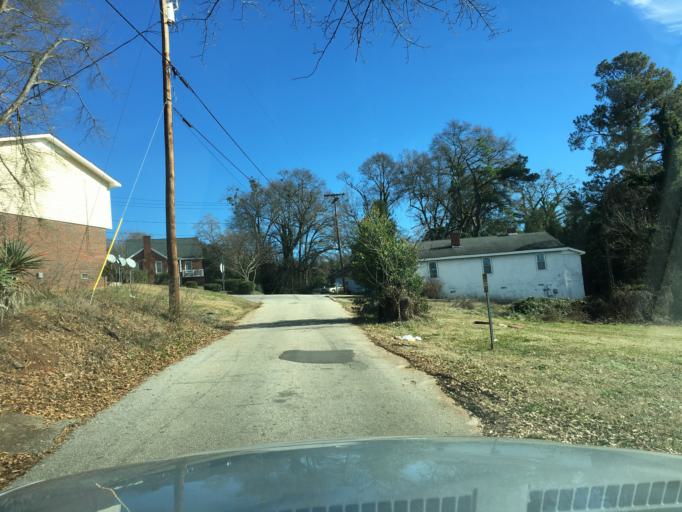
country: US
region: South Carolina
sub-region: Greenville County
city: Greenville
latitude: 34.8581
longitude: -82.3831
